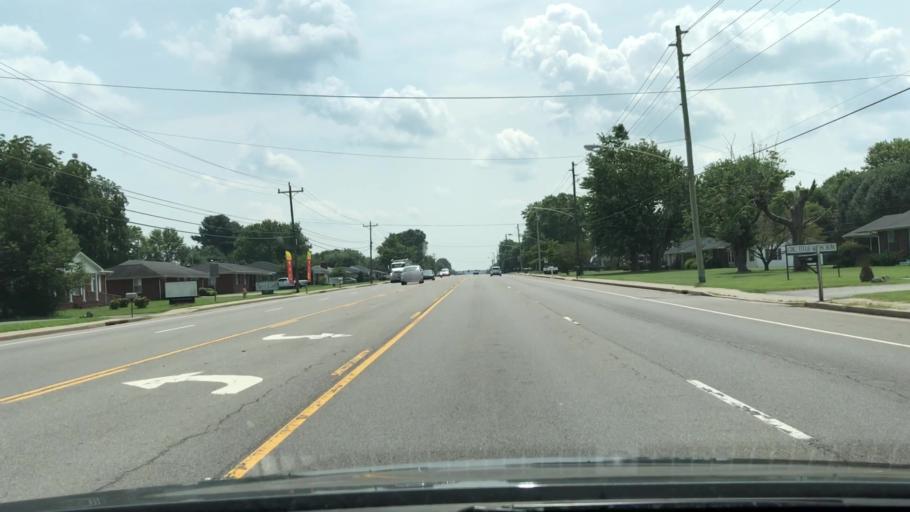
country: US
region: Tennessee
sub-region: Sumner County
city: Portland
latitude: 36.5657
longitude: -86.5111
